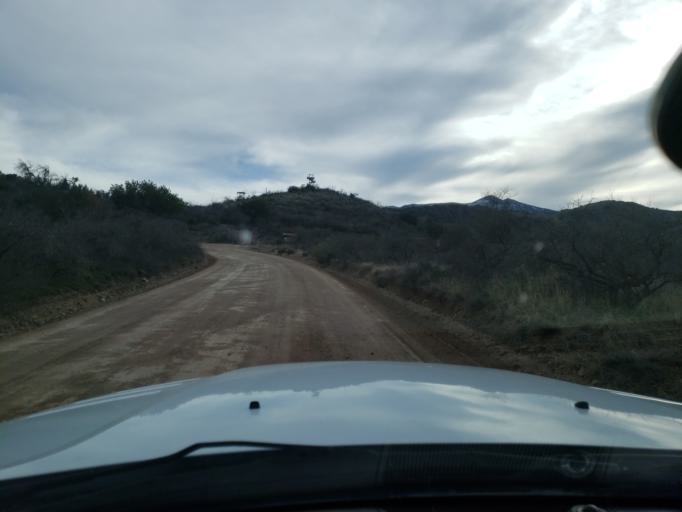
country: US
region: Arizona
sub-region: Pinal County
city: Oracle
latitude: 32.5502
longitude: -110.7081
